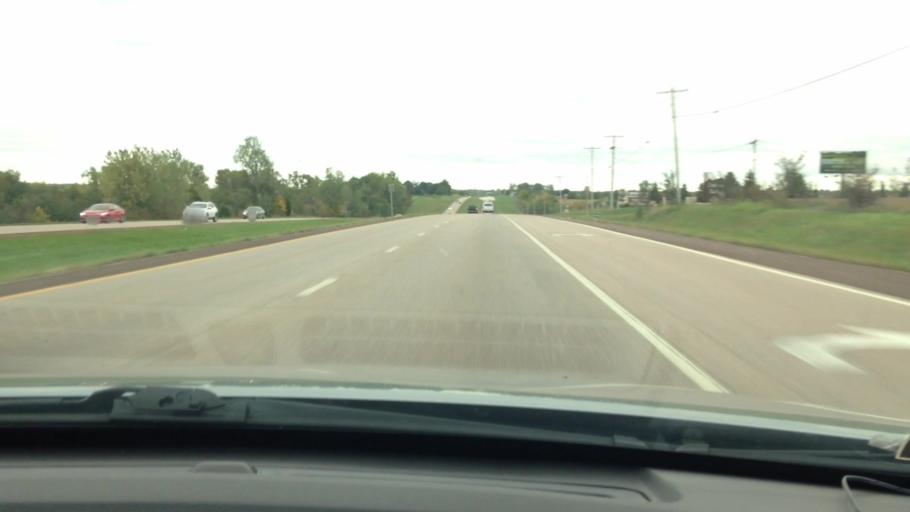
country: US
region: Kansas
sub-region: Leavenworth County
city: Basehor
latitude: 39.1689
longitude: -94.9007
